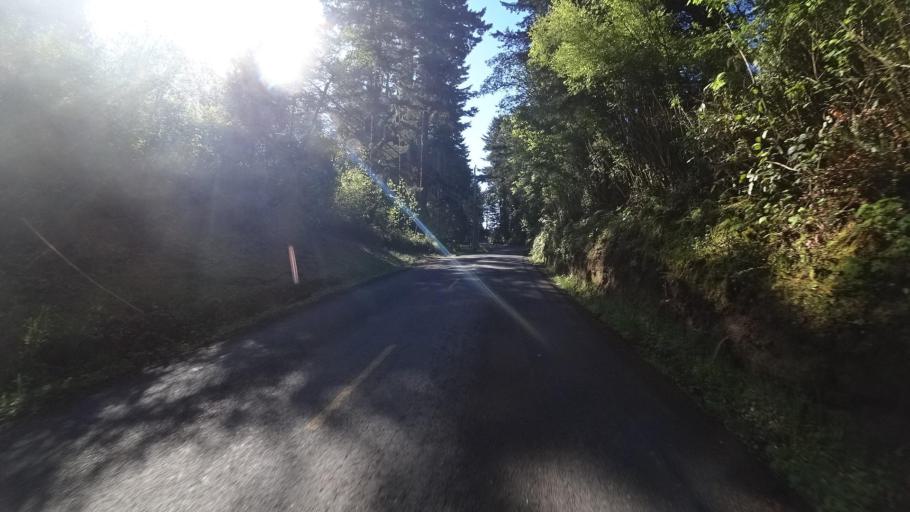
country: US
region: California
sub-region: Humboldt County
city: McKinleyville
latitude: 40.9815
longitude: -124.0980
